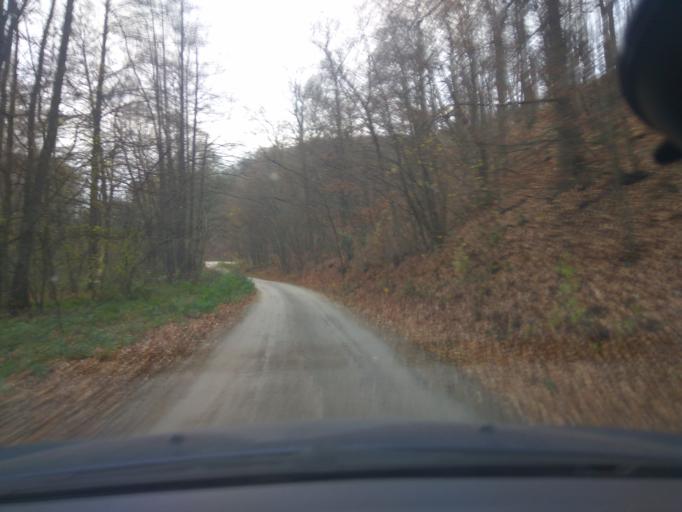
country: SK
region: Trnavsky
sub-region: Okres Trnava
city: Piestany
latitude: 48.6072
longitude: 17.9270
